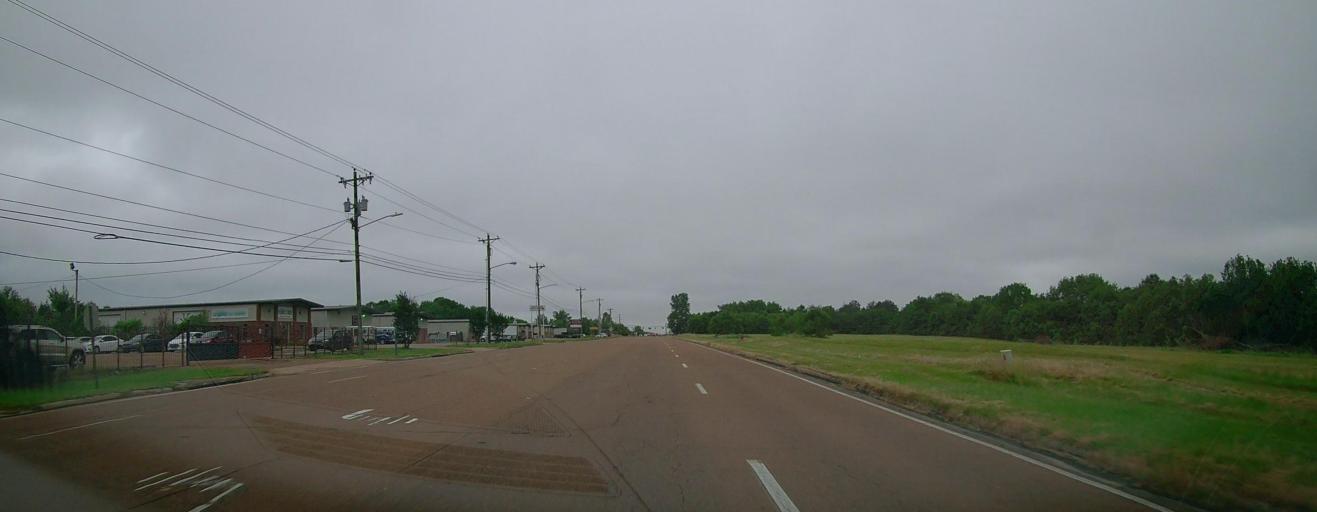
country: US
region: Mississippi
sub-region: De Soto County
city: Olive Branch
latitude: 34.9381
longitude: -89.7950
